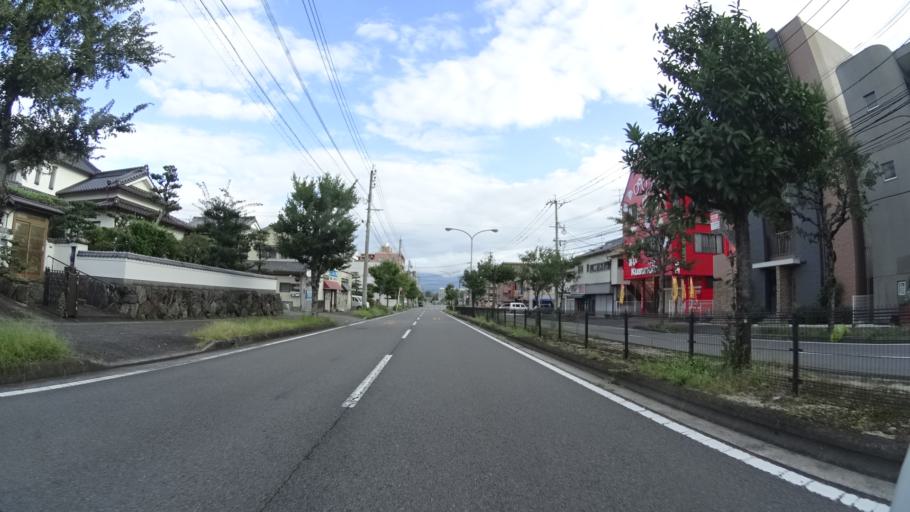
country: JP
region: Oita
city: Beppu
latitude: 33.2976
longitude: 131.4954
